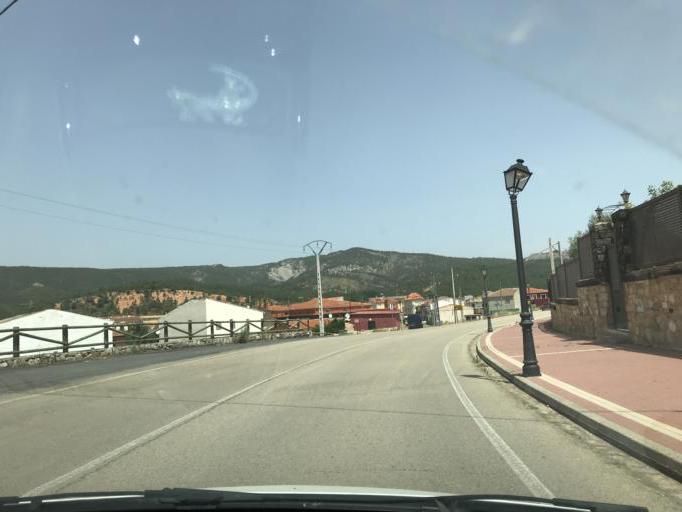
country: ES
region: Castille-La Mancha
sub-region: Provincia de Cuenca
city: Canamares
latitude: 40.4492
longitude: -2.2387
